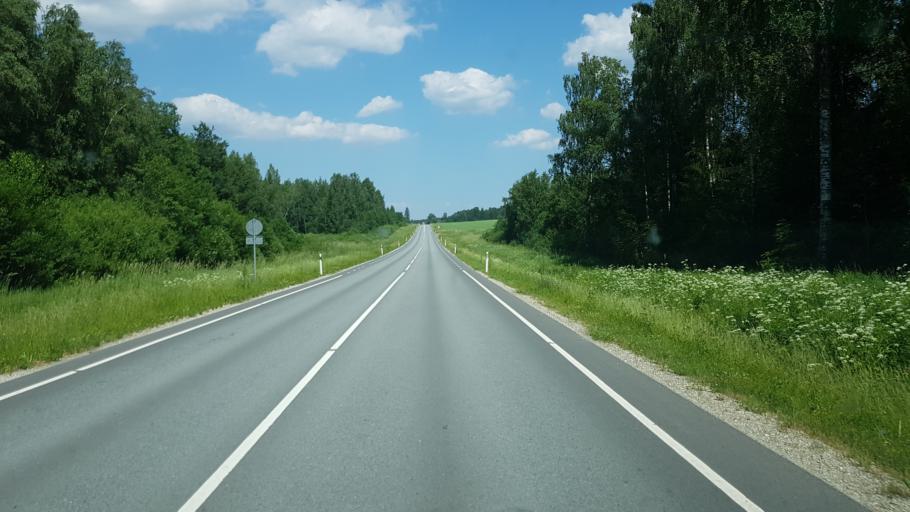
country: EE
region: Tartu
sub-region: Alatskivi vald
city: Kallaste
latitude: 58.5539
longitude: 27.1149
